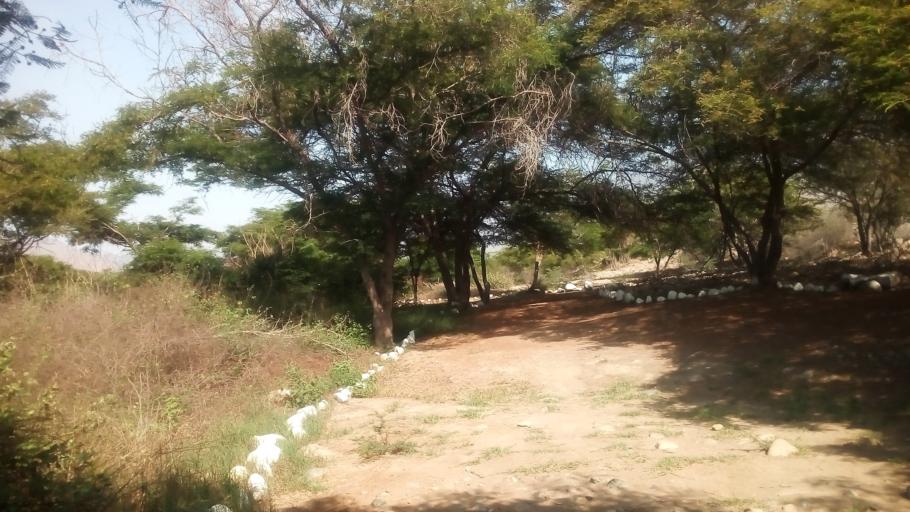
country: PE
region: Lima
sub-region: Huaura
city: Vegueta
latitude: -10.8928
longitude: -77.5137
